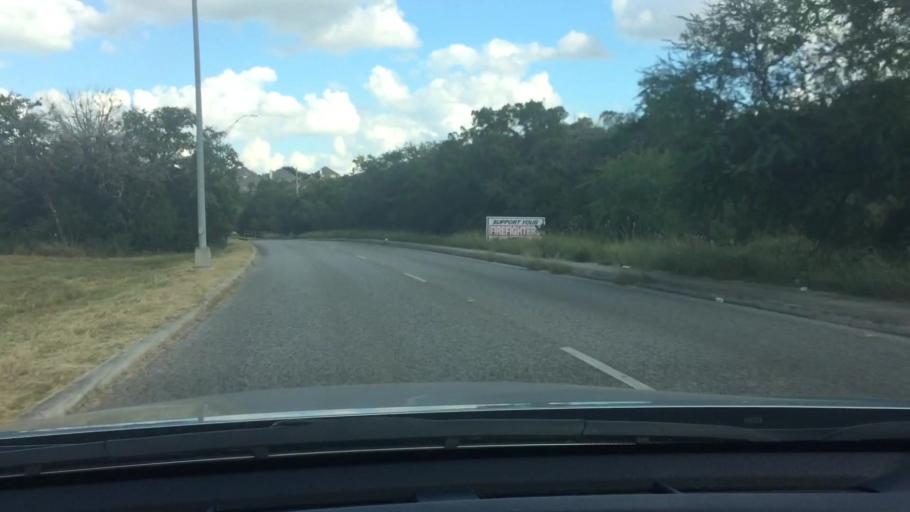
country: US
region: Texas
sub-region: Bexar County
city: Hollywood Park
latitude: 29.6348
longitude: -98.4504
